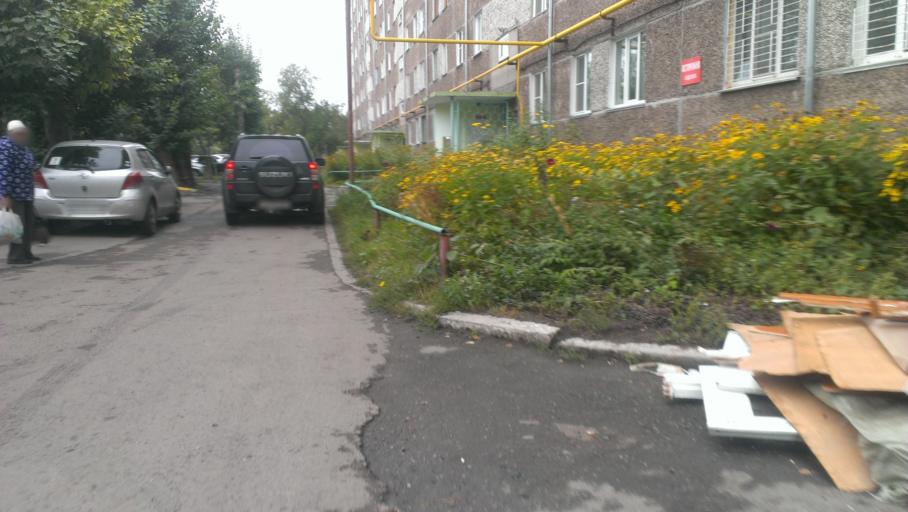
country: RU
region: Altai Krai
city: Novosilikatnyy
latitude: 53.3665
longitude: 83.6815
